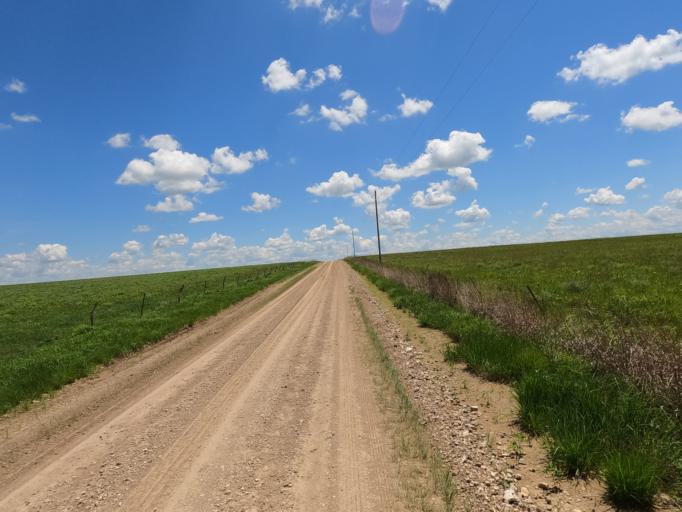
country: US
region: Kansas
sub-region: Chase County
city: Cottonwood Falls
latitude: 38.2167
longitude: -96.7442
